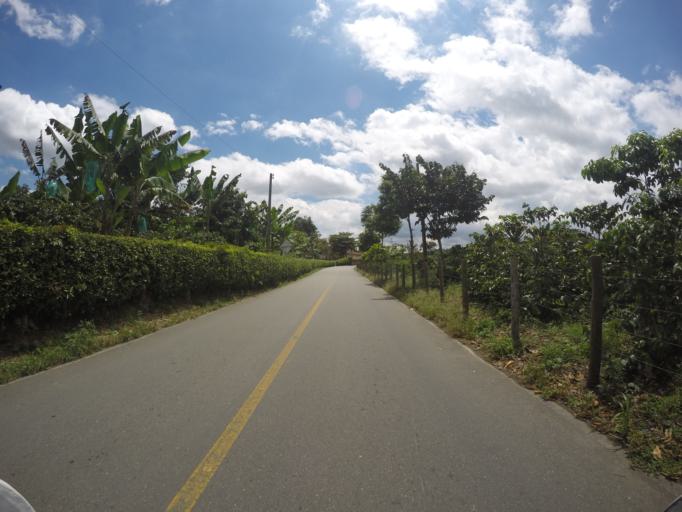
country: CO
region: Quindio
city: Quimbaya
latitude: 4.6259
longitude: -75.7453
